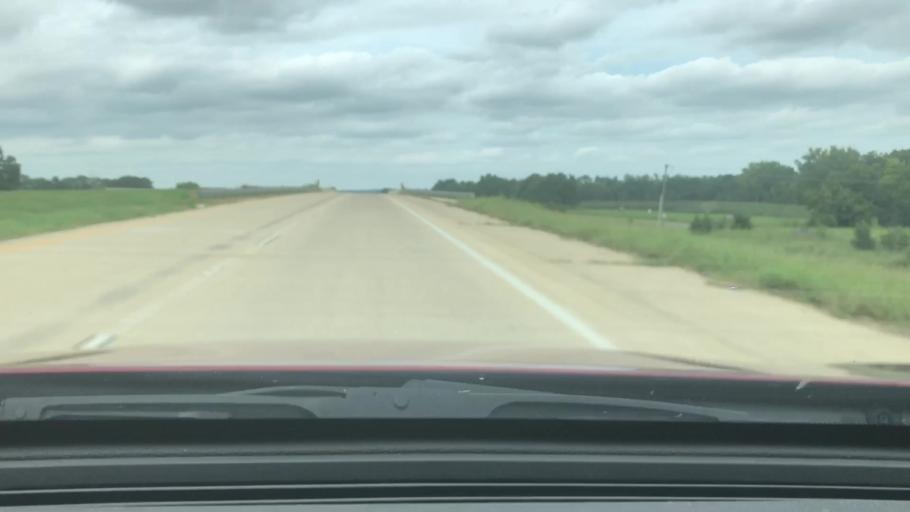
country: US
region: Louisiana
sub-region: Caddo Parish
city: Oil City
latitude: 32.7470
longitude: -93.8810
